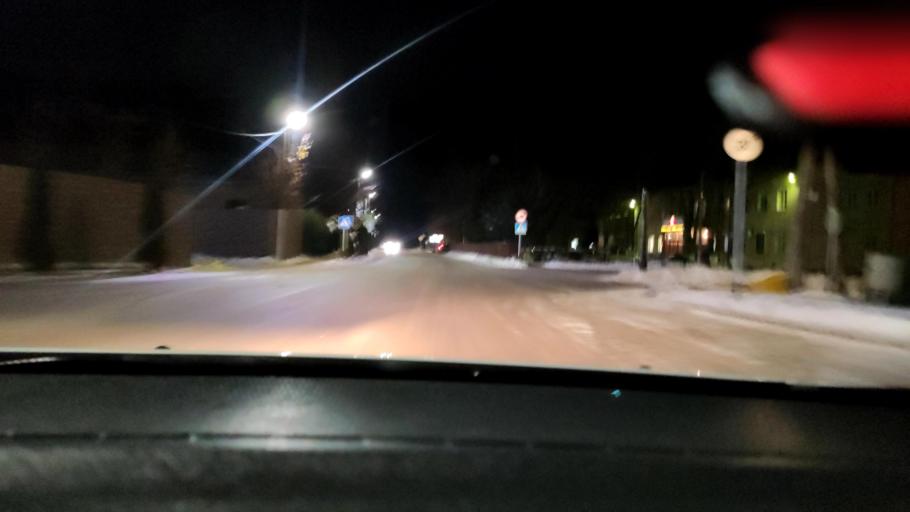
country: RU
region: Voronezj
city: Ramon'
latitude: 51.9143
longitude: 39.3343
